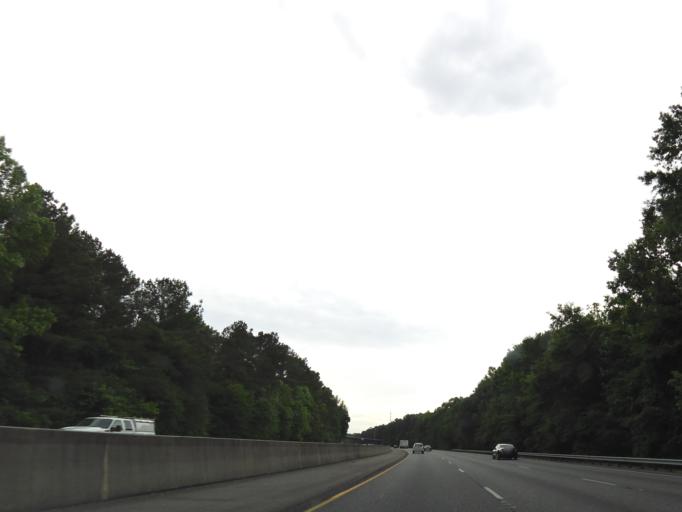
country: US
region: Georgia
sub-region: Bibb County
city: West Point
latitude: 32.8554
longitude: -83.7435
